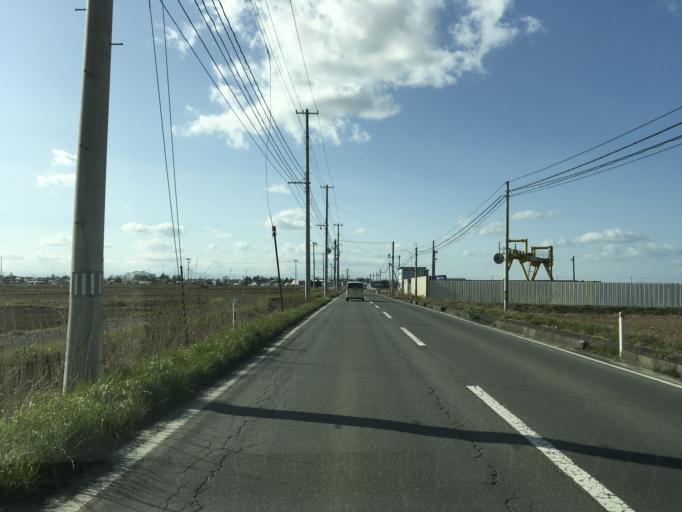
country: JP
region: Miyagi
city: Wakuya
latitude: 38.6685
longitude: 141.2642
